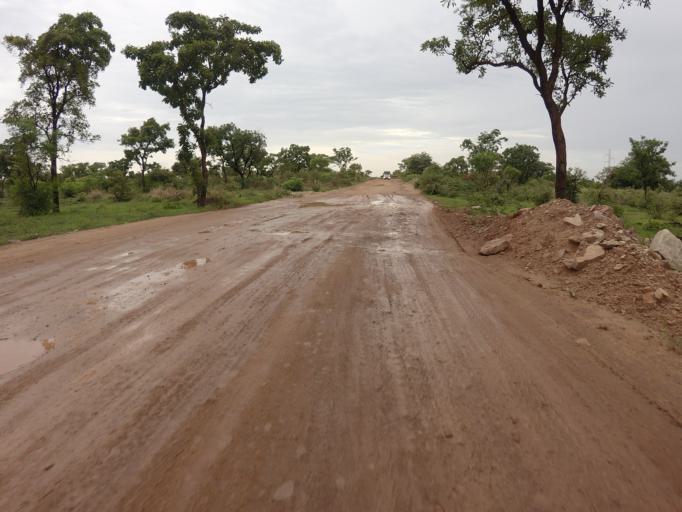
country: GH
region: Upper East
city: Bolgatanga
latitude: 10.8733
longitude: -0.6408
